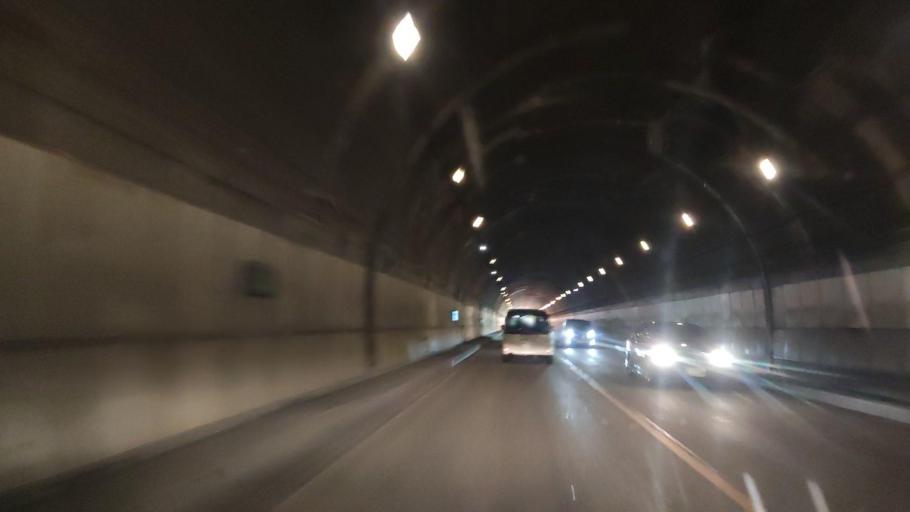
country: JP
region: Aomori
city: Aomori Shi
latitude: 40.8579
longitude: 140.8417
